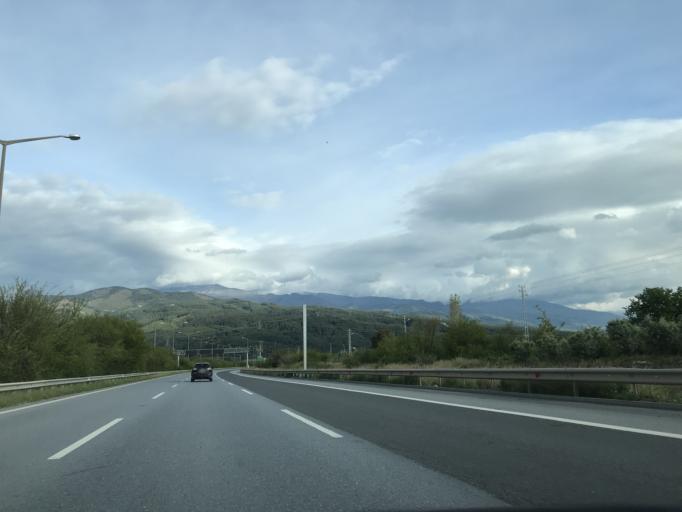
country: TR
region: Hatay
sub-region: Doertyol Ilcesi
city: Dortyol
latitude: 36.8966
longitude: 36.2306
